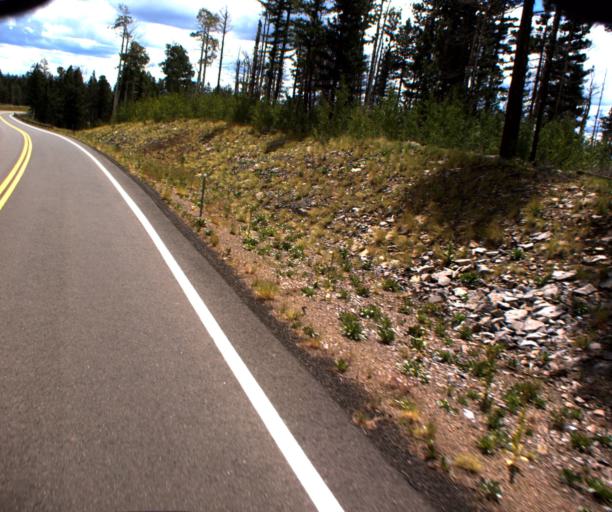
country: US
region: Arizona
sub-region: Apache County
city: Eagar
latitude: 33.9279
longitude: -109.4629
